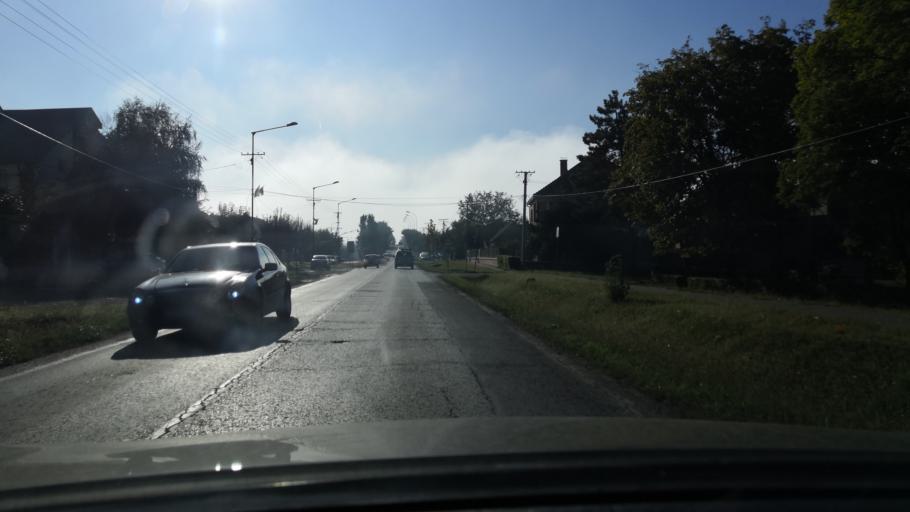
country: RS
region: Autonomna Pokrajina Vojvodina
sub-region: Sremski Okrug
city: Ingija
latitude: 45.0382
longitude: 20.0913
